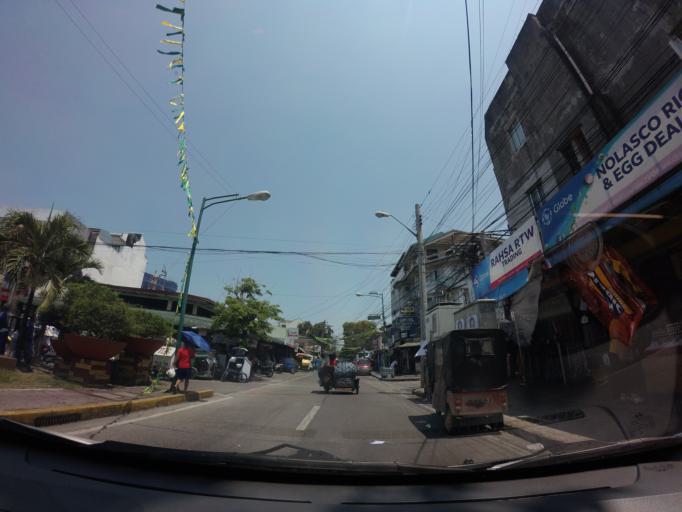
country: PH
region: Metro Manila
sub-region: Makati City
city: Makati City
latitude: 14.5617
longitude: 121.0023
